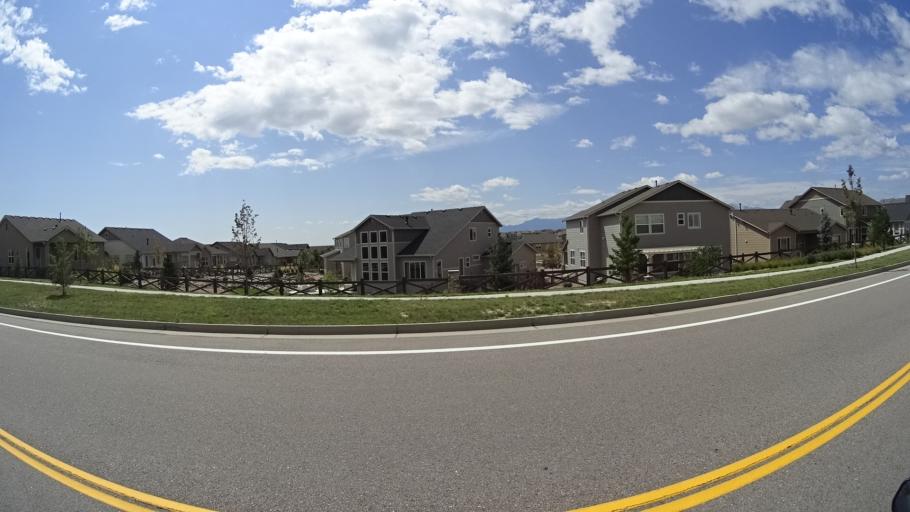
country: US
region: Colorado
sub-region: El Paso County
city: Cimarron Hills
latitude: 38.9310
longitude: -104.6659
